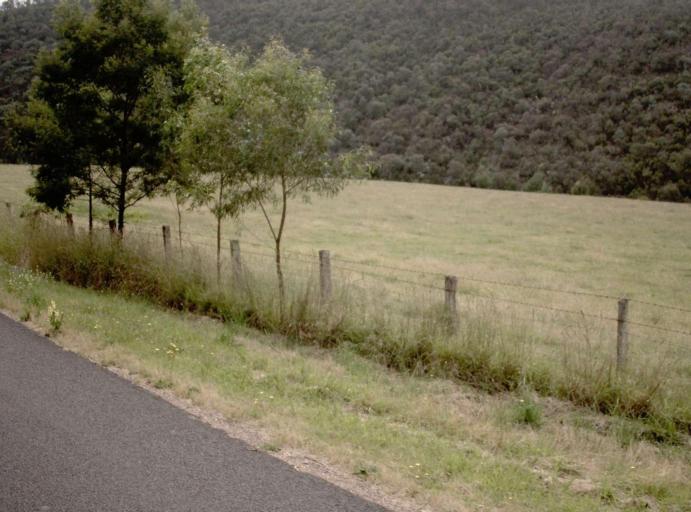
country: AU
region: Victoria
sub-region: Wellington
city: Heyfield
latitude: -37.7936
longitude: 146.6783
